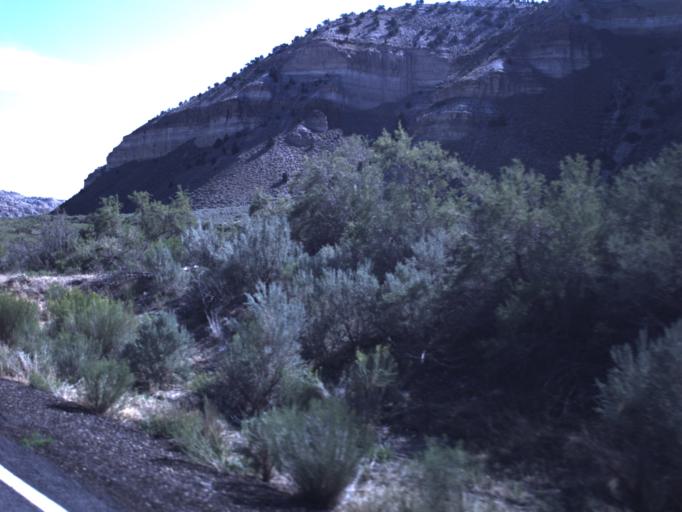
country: US
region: Utah
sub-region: Duchesne County
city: Duchesne
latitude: 40.0824
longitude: -110.4986
